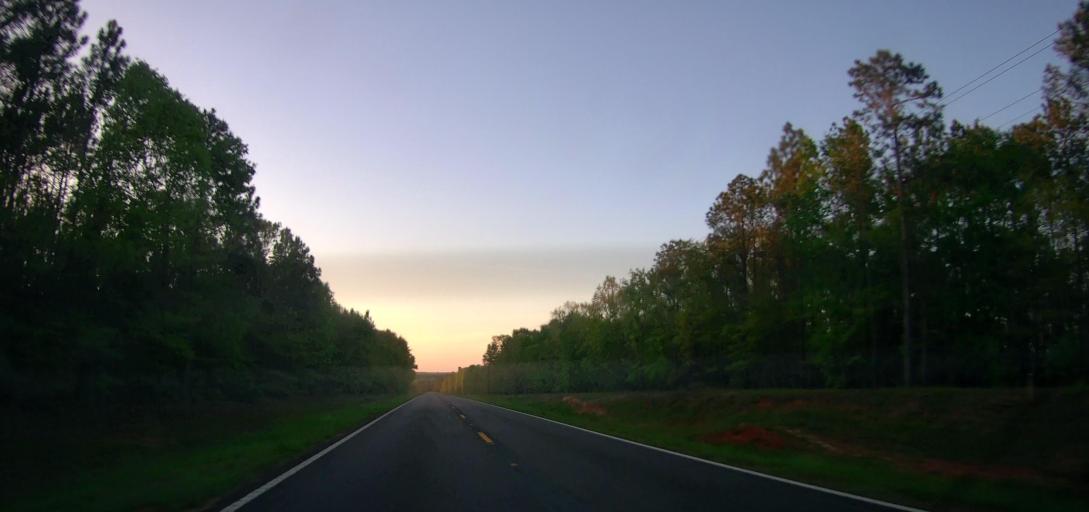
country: US
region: Georgia
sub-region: Marion County
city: Buena Vista
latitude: 32.4119
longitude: -84.5847
